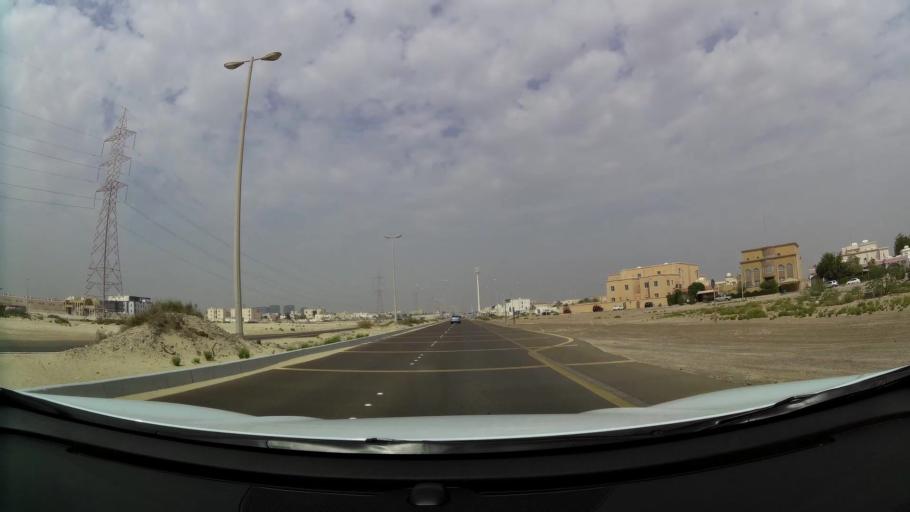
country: AE
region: Abu Dhabi
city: Abu Dhabi
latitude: 24.3188
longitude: 54.6329
